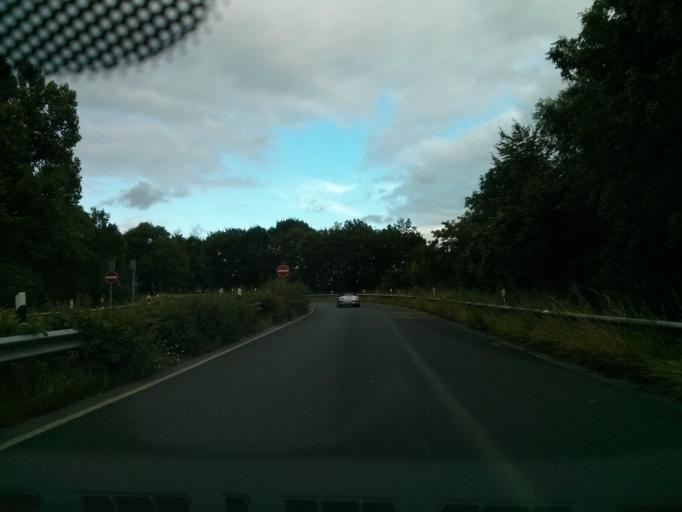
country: DE
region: North Rhine-Westphalia
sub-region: Regierungsbezirk Dusseldorf
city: Moers
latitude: 51.4351
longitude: 6.6103
